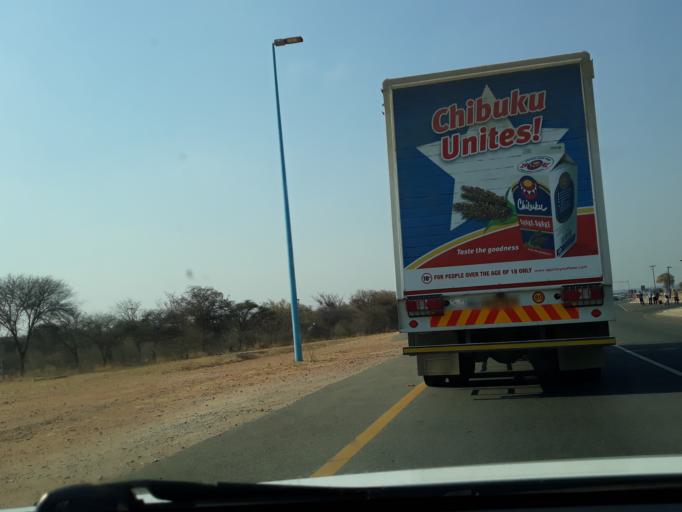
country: BW
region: Central
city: Tonota
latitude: -21.4251
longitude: 27.4416
